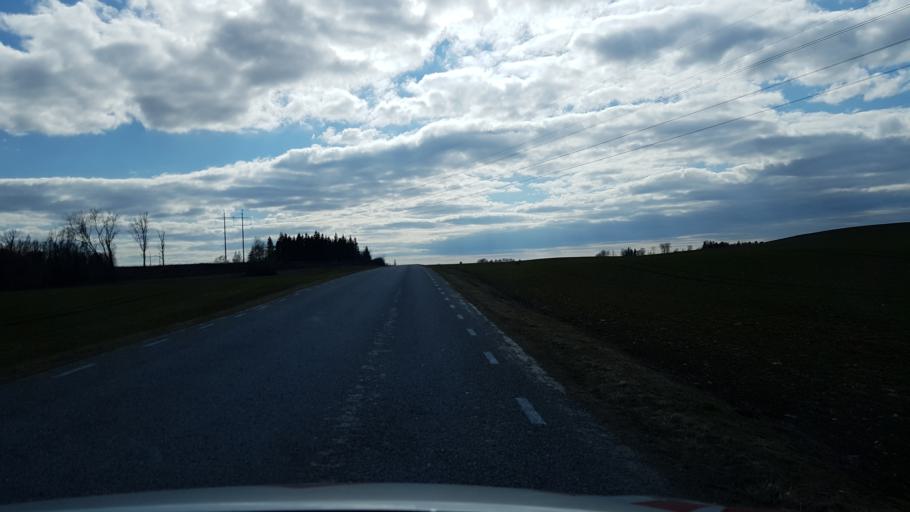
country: EE
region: Laeaene-Virumaa
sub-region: Kadrina vald
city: Kadrina
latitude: 59.3029
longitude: 26.2219
